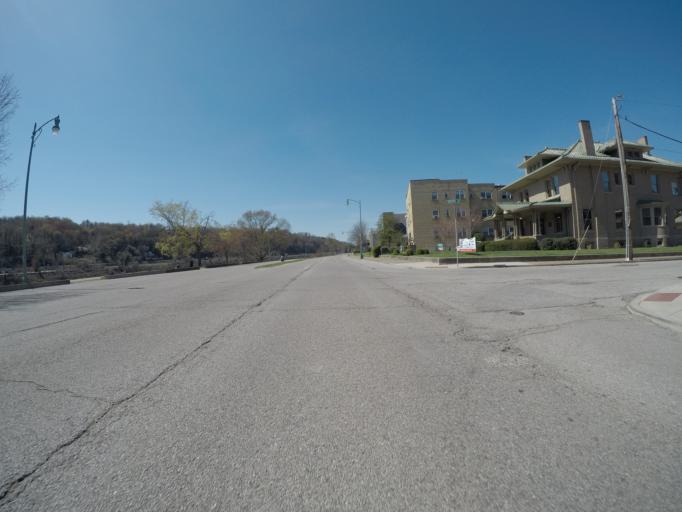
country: US
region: West Virginia
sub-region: Kanawha County
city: Charleston
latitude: 38.3406
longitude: -81.6262
